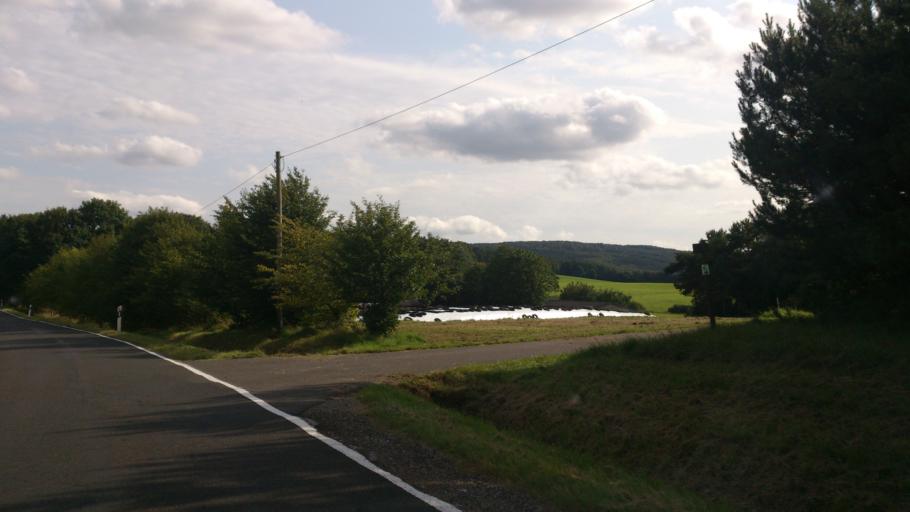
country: DE
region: Rheinland-Pfalz
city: Nohn
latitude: 50.3226
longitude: 6.7856
